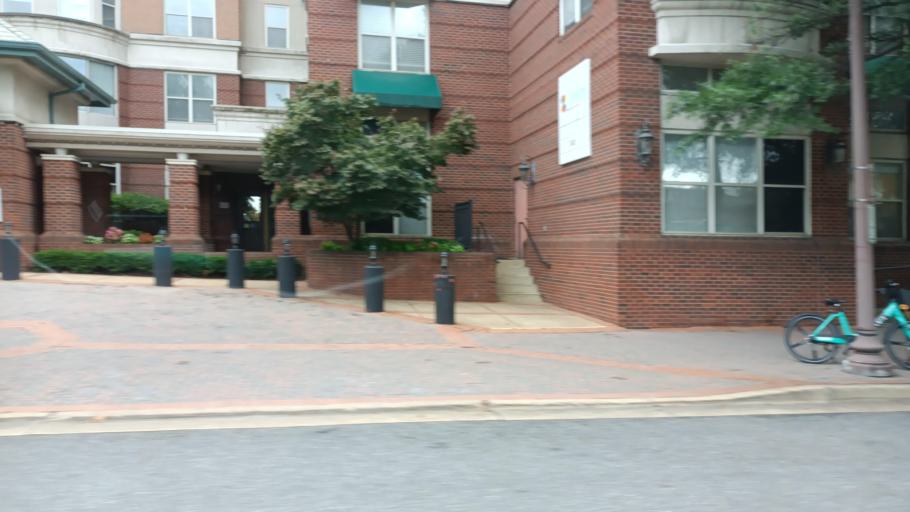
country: US
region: Virginia
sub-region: Arlington County
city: Arlington
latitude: 38.8809
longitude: -77.1048
